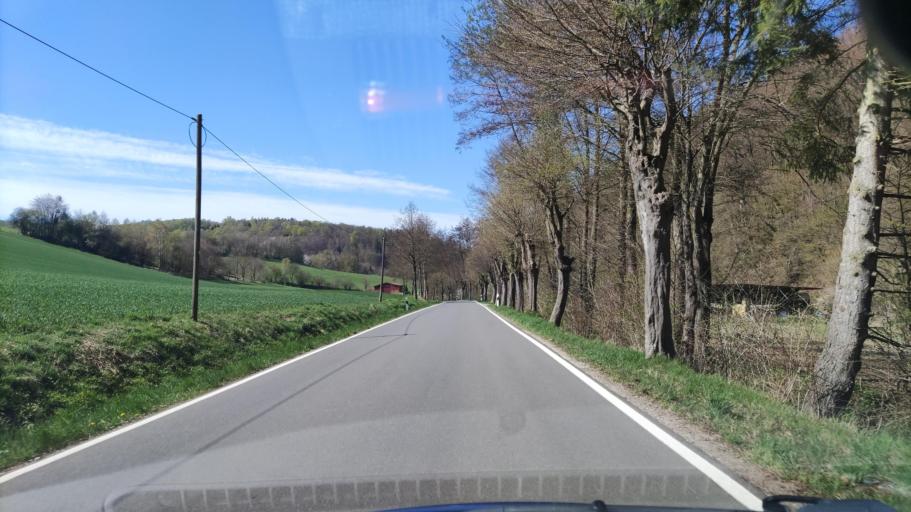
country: DE
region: Lower Saxony
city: Eimen
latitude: 51.9144
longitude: 9.7779
